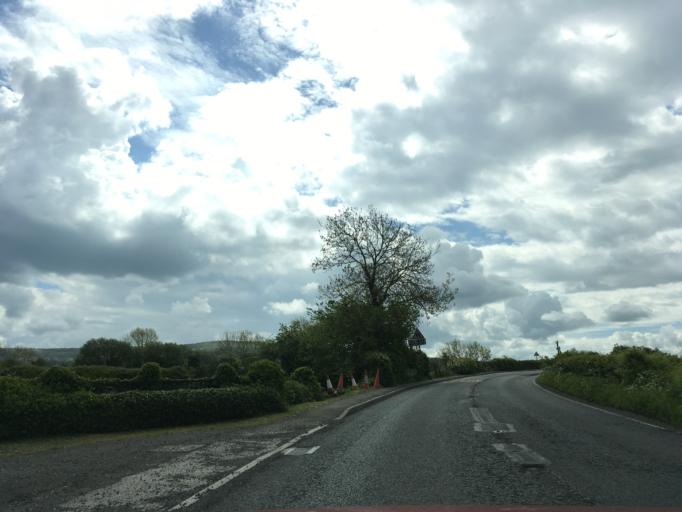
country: GB
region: England
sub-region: Gloucestershire
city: Stonehouse
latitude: 51.7723
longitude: -2.2843
